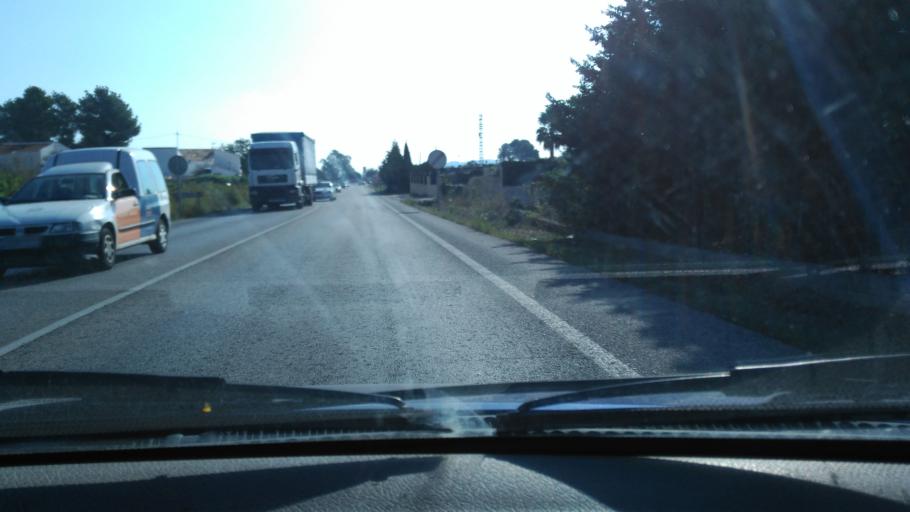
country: ES
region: Valencia
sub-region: Provincia de Alicante
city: Gata de Gorgos
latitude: 38.7839
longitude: 0.0870
